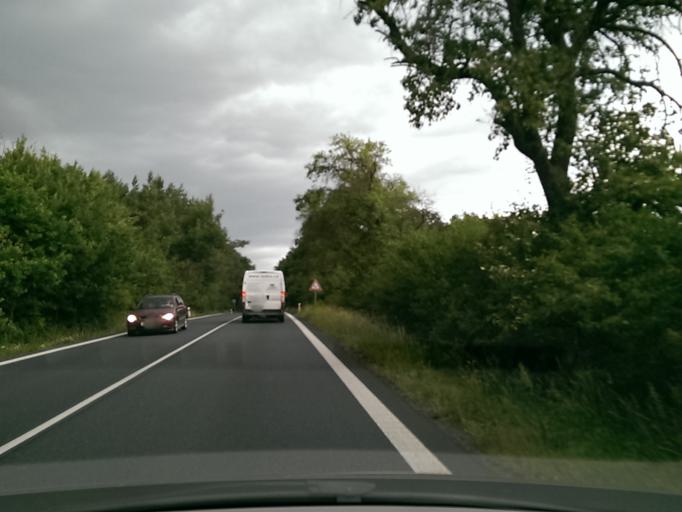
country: CZ
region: Central Bohemia
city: Loucen
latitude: 50.2594
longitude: 14.9809
